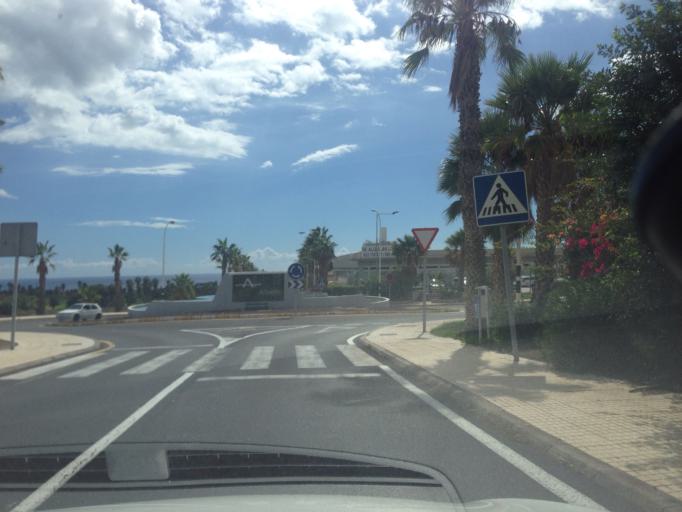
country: ES
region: Canary Islands
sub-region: Provincia de Santa Cruz de Tenerife
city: Las Rosas
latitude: 28.0434
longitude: -16.6119
